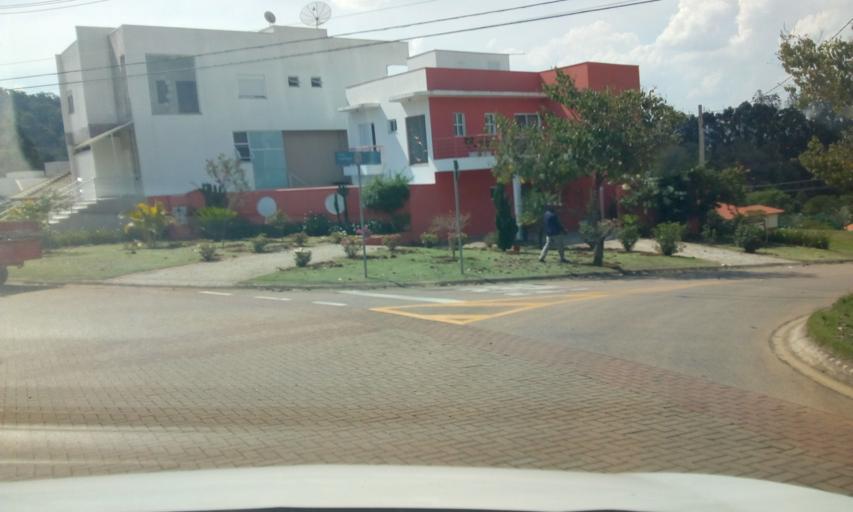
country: BR
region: Sao Paulo
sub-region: Itupeva
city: Itupeva
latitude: -23.1382
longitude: -47.0498
